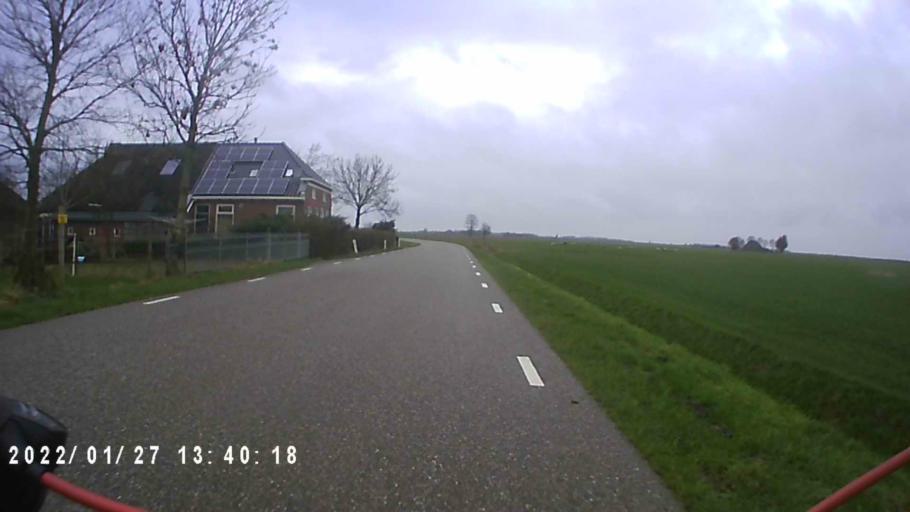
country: NL
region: Friesland
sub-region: Gemeente Kollumerland en Nieuwkruisland
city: Kollum
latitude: 53.2999
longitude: 6.2181
